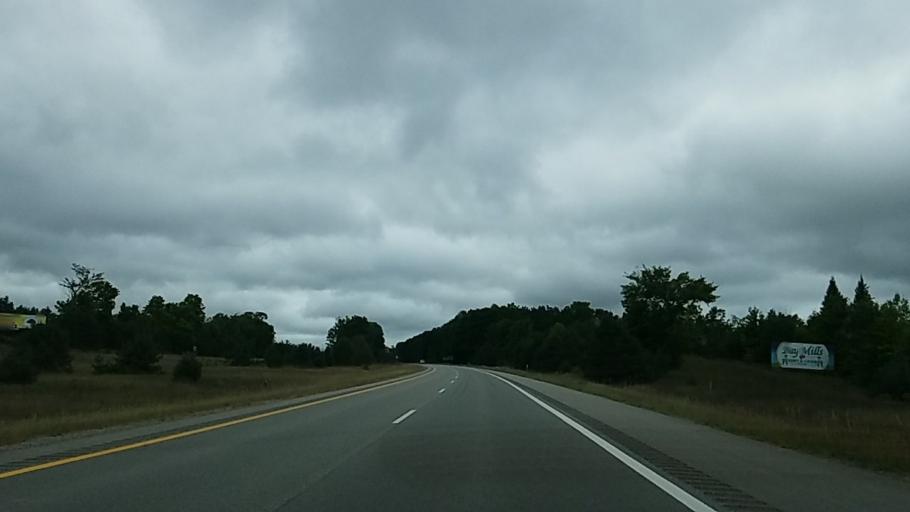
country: US
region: Michigan
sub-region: Otsego County
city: Gaylord
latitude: 45.1587
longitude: -84.6659
